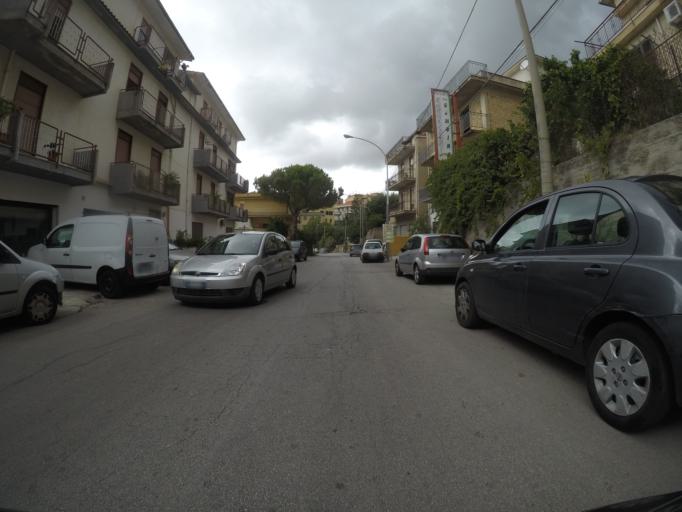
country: IT
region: Sicily
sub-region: Palermo
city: Montelepre
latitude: 38.0924
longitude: 13.1749
